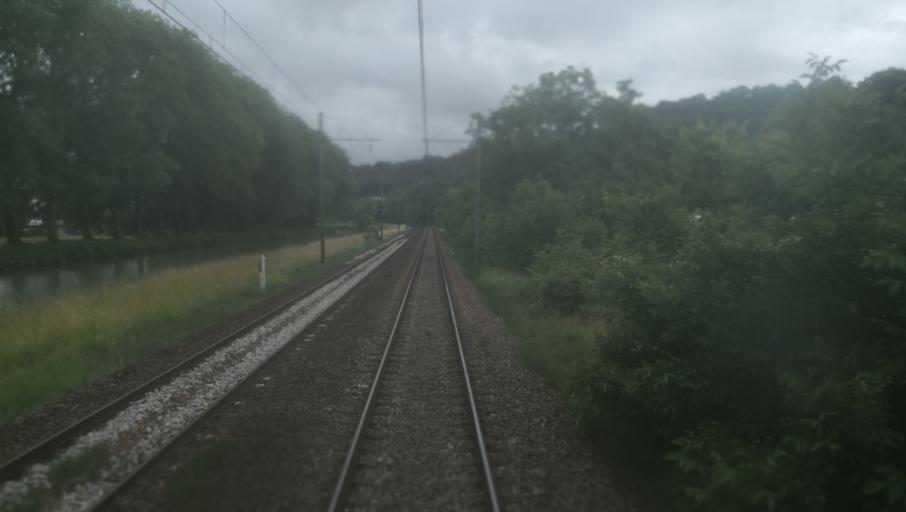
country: FR
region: Midi-Pyrenees
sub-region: Departement du Tarn-et-Garonne
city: Saint-Nicolas-de-la-Grave
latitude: 44.0912
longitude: 0.9979
